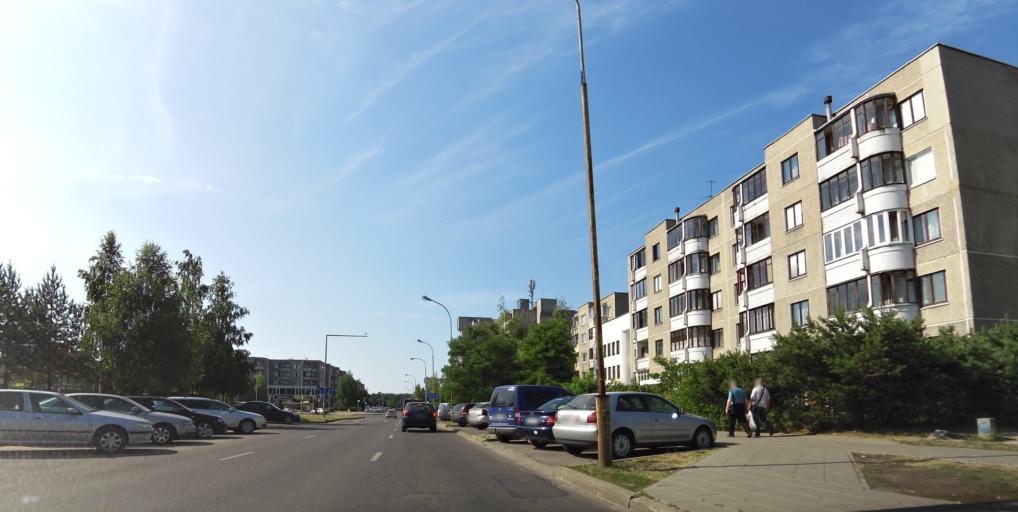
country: LT
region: Vilnius County
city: Pilaite
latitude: 54.7082
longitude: 25.1866
